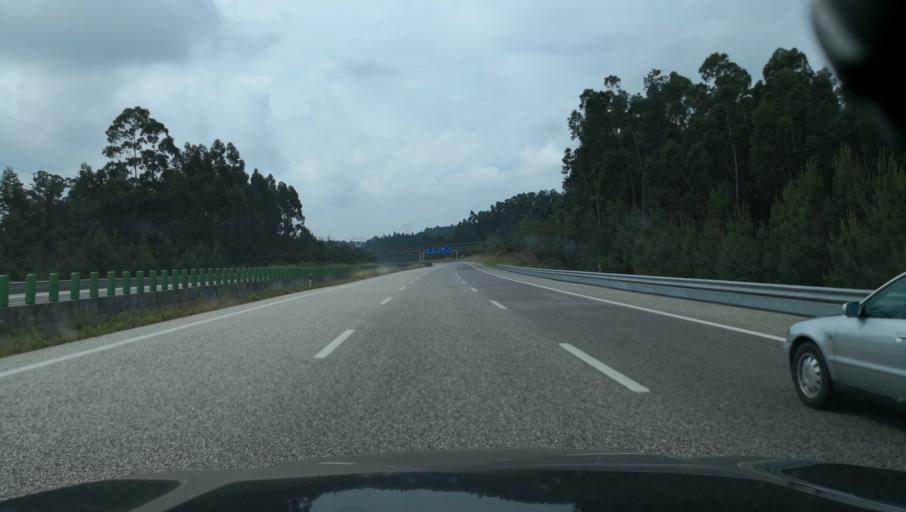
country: PT
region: Leiria
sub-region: Pombal
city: Lourical
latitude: 39.9602
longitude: -8.7752
